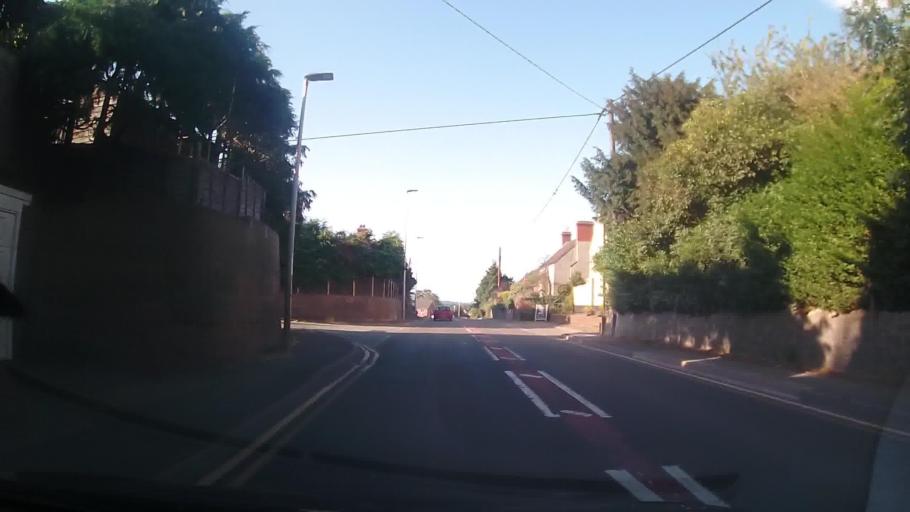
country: GB
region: England
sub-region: Shropshire
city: Bayston Hill
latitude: 52.6738
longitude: -2.7608
